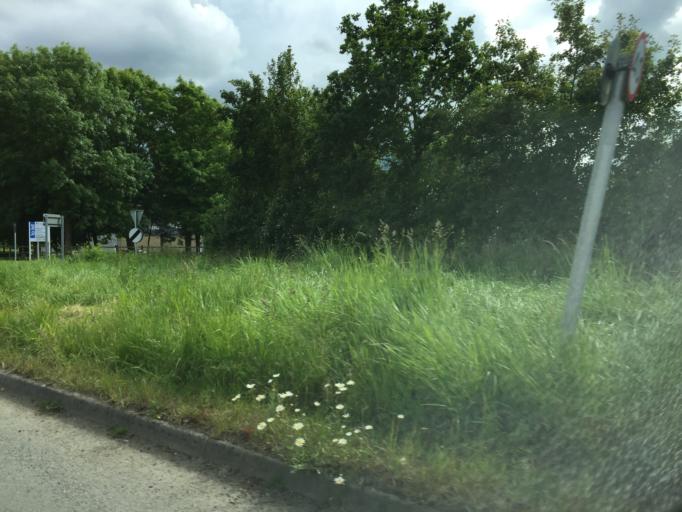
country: GB
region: England
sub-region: Wiltshire
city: Cricklade
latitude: 51.6314
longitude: -1.8786
